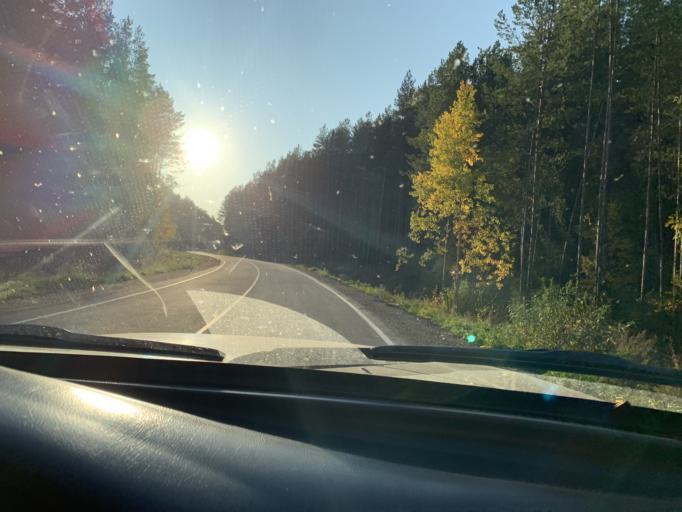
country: RU
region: Sverdlovsk
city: Verkhneye Dubrovo
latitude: 56.8677
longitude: 61.0719
